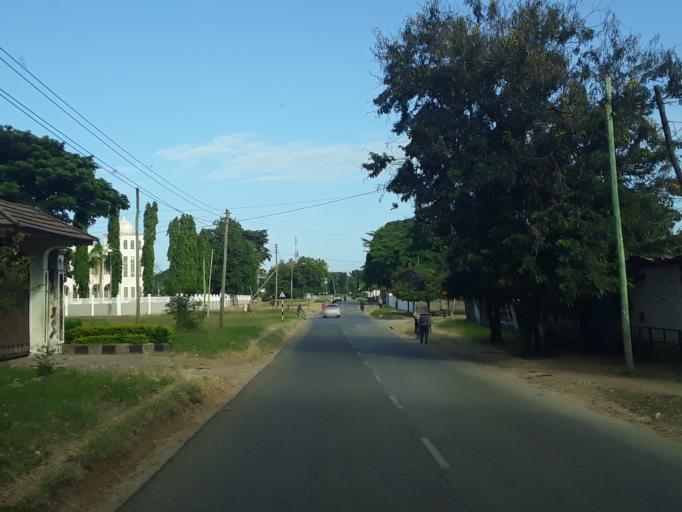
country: TZ
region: Tanga
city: Tanga
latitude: -5.0728
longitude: 39.1112
